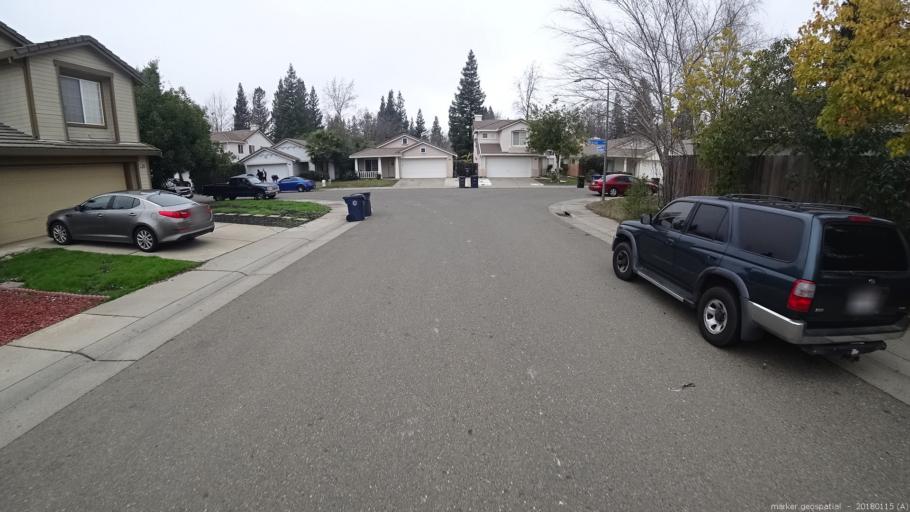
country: US
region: California
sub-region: Sacramento County
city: Rancho Cordova
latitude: 38.5799
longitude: -121.2934
